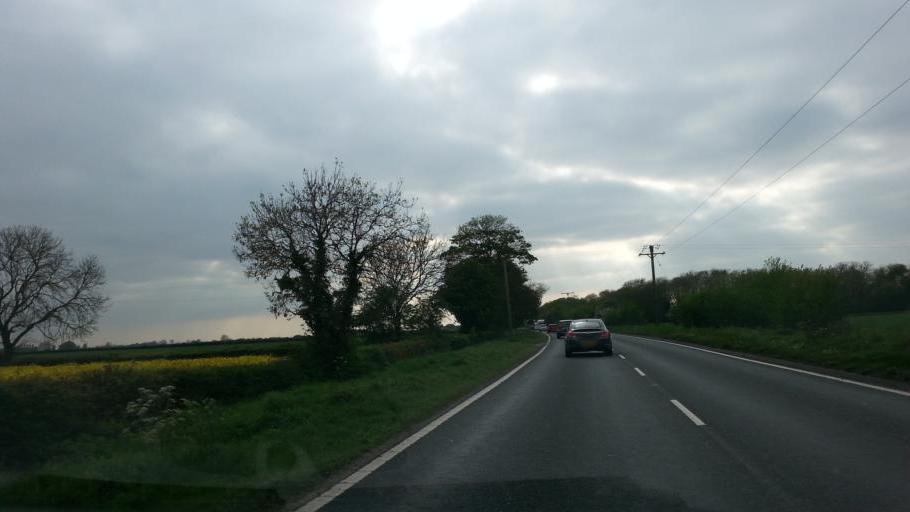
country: GB
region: England
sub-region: Nottinghamshire
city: South Collingham
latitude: 53.0700
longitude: -0.6628
